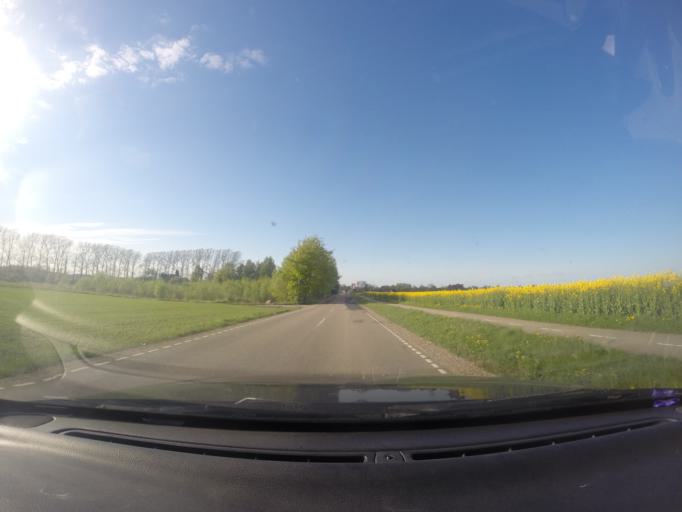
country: DK
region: Capital Region
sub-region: Hoje-Taastrup Kommune
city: Taastrup
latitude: 55.6759
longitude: 12.2534
